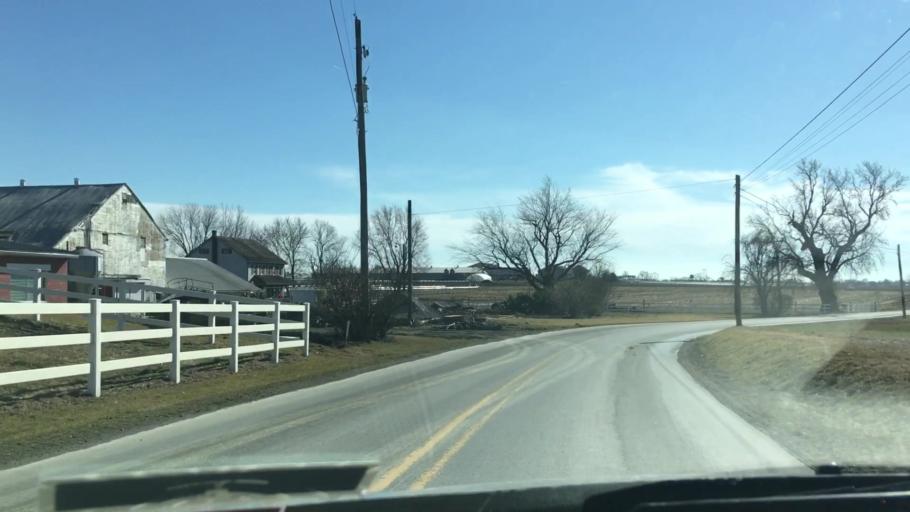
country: US
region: Pennsylvania
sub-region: Lancaster County
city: New Holland
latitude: 40.1226
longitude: -76.1292
